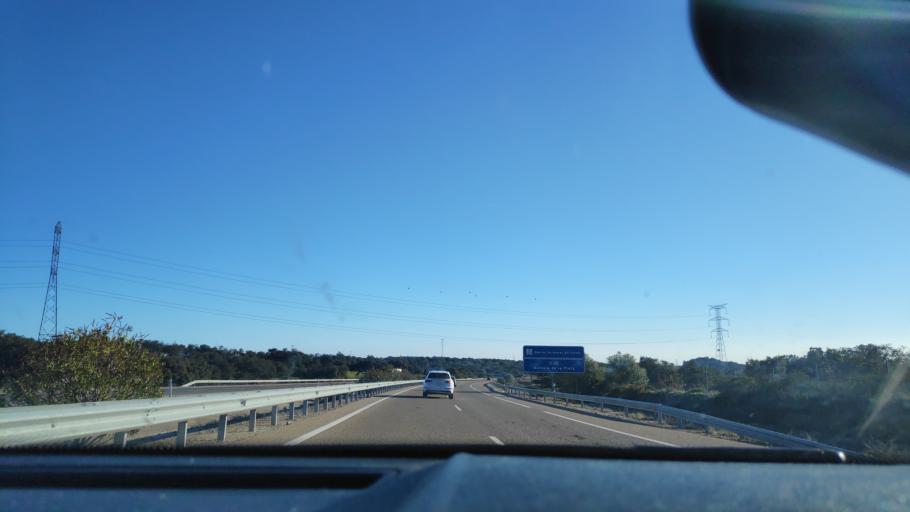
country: ES
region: Andalusia
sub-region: Provincia de Sevilla
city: Gerena
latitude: 37.6154
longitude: -6.1255
